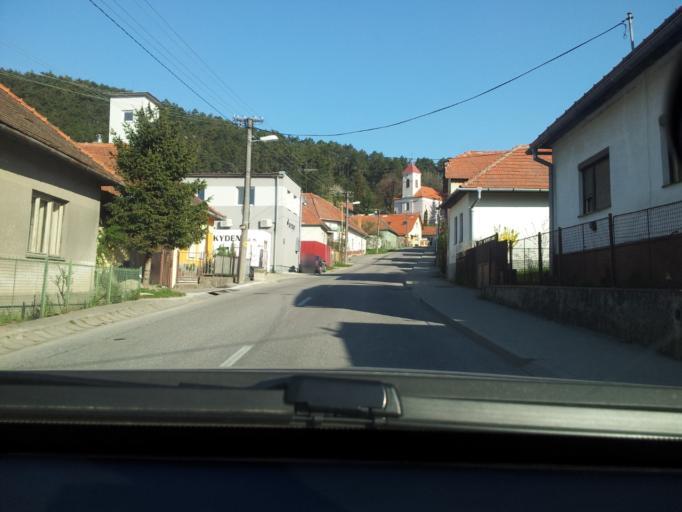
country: SK
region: Nitriansky
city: Zlate Moravce
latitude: 48.5058
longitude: 18.4195
